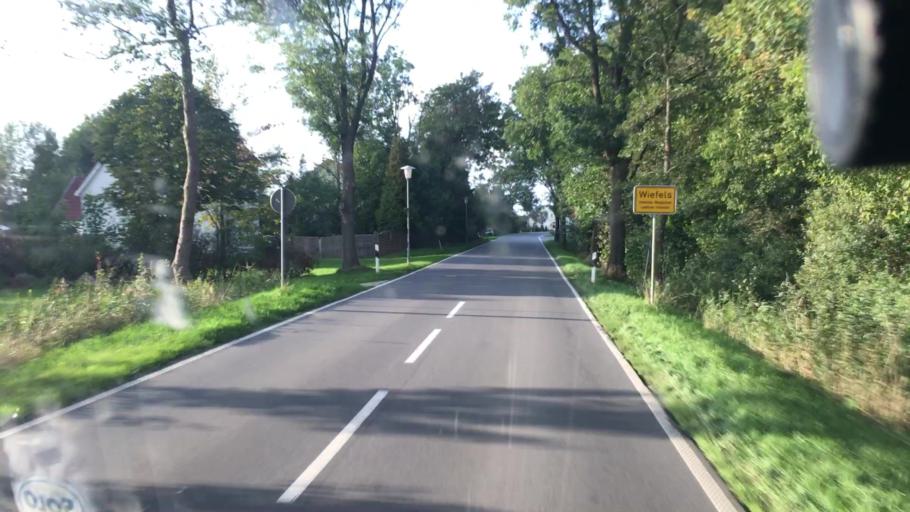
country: DE
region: Lower Saxony
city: Jever
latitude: 53.5952
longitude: 7.8692
